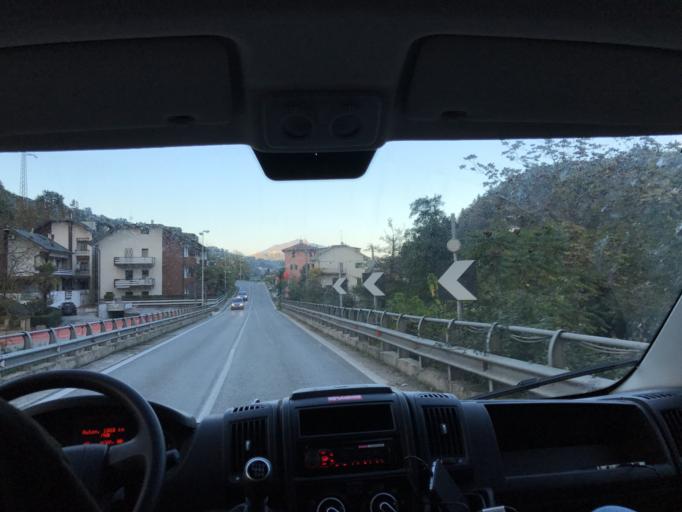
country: IT
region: The Marches
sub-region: Provincia di Ascoli Piceno
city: Marsia
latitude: 42.8223
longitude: 13.5082
